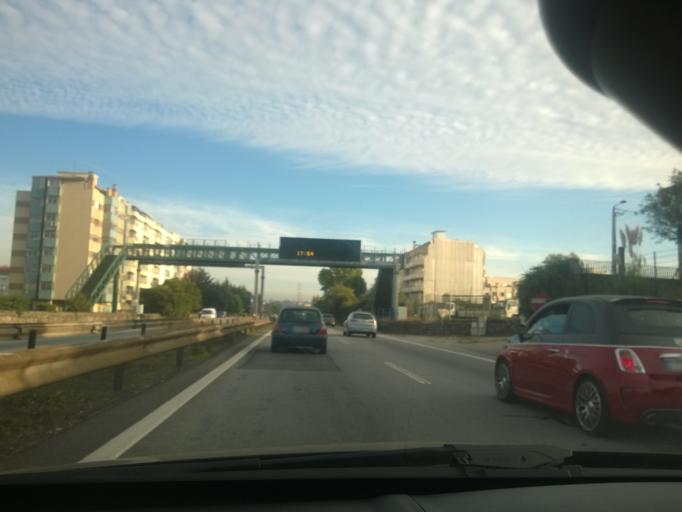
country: PT
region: Porto
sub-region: Matosinhos
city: Senhora da Hora
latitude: 41.1885
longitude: -8.6263
